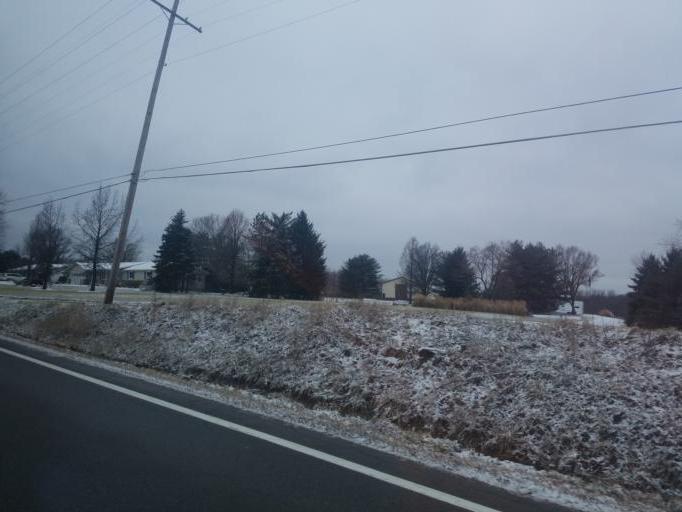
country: US
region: Ohio
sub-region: Licking County
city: Johnstown
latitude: 40.1705
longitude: -82.7129
